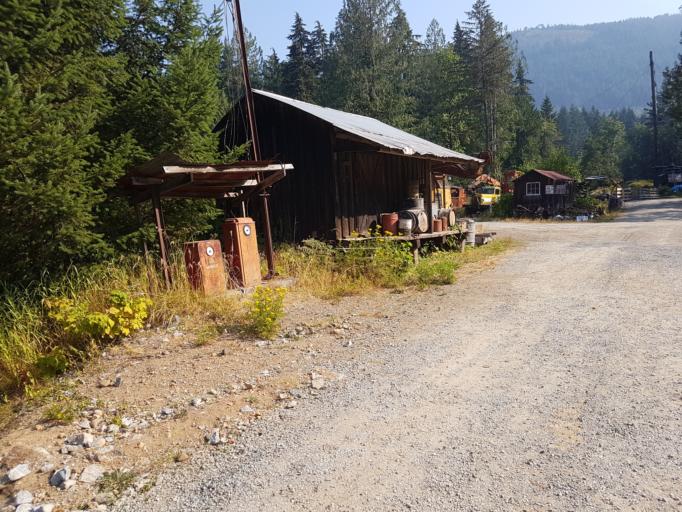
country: CA
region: British Columbia
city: Port Alberni
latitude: 49.3113
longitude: -124.8259
